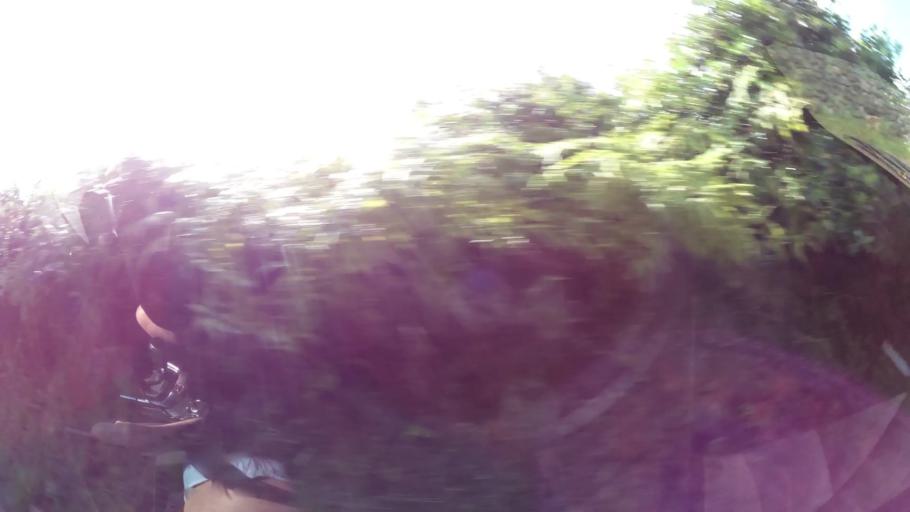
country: CO
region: Valle del Cauca
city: Cali
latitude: 3.4290
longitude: -76.5640
